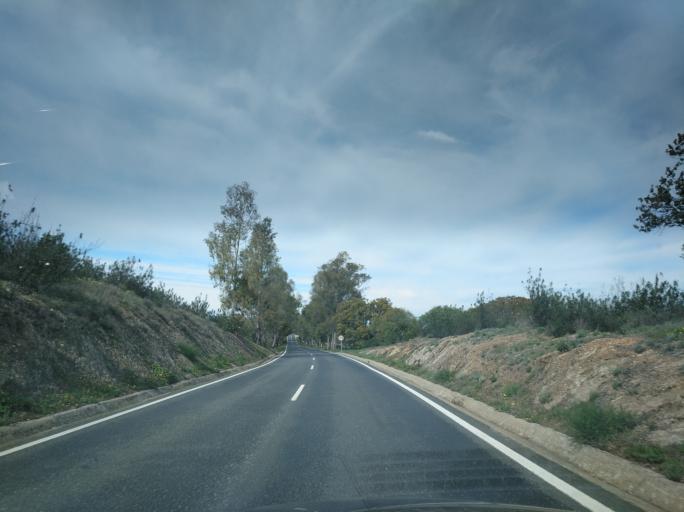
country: PT
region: Beja
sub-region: Mertola
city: Mertola
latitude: 37.7122
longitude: -7.7543
